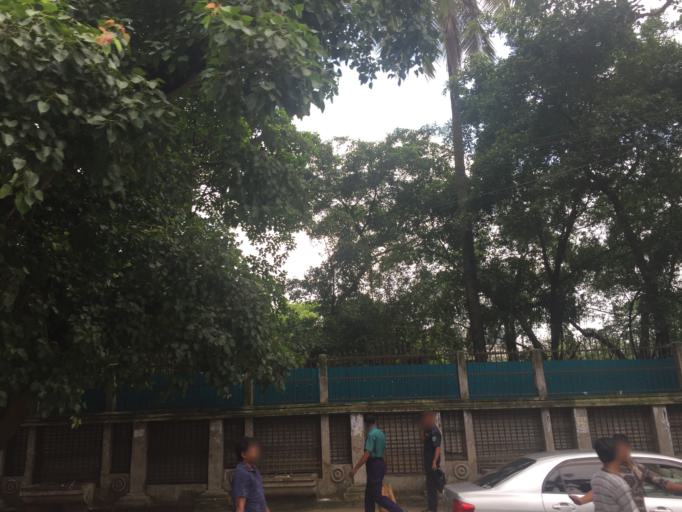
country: BD
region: Dhaka
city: Paltan
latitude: 23.7248
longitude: 90.4071
